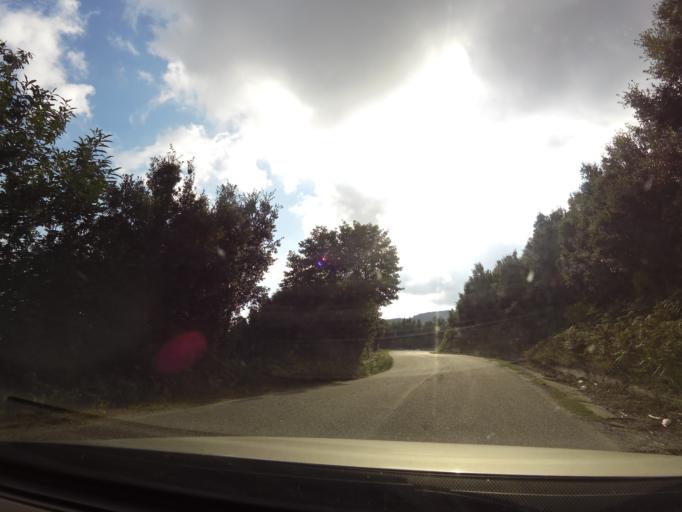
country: IT
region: Calabria
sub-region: Provincia di Vibo-Valentia
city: Nardodipace
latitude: 38.4758
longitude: 16.3880
